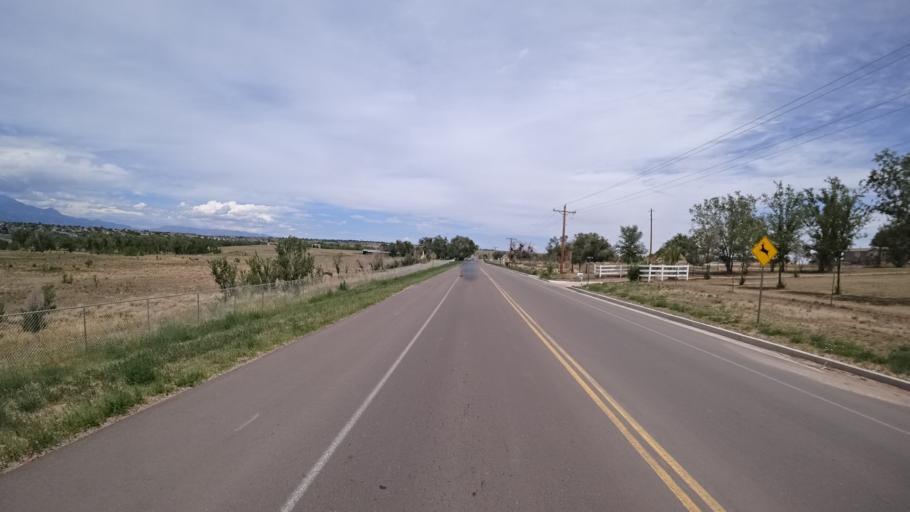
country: US
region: Colorado
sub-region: El Paso County
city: Fountain
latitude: 38.6955
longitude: -104.6737
